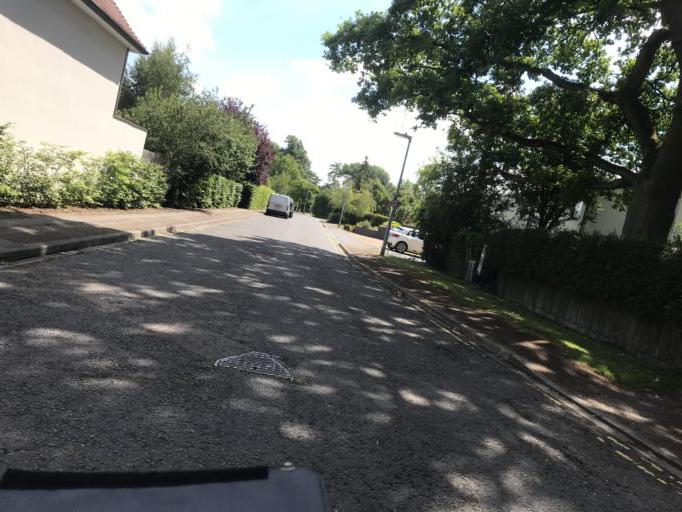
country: GB
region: England
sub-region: Cambridgeshire
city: Cambridge
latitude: 52.1860
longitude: 0.1243
